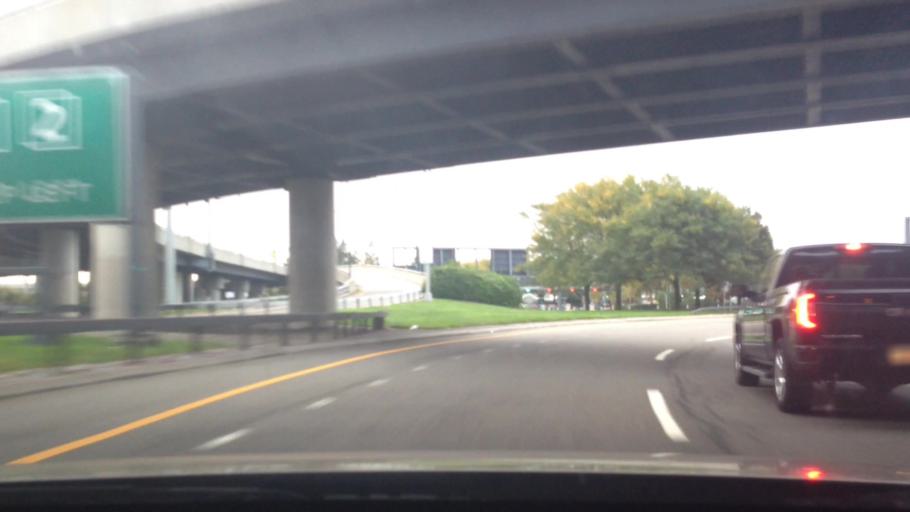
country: US
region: New York
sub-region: Nassau County
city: Inwood
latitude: 40.6448
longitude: -73.7870
